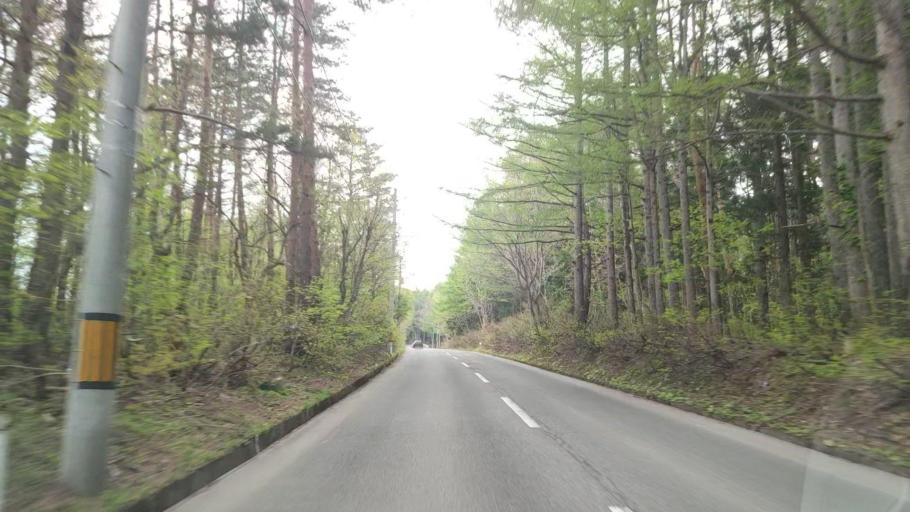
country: JP
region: Aomori
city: Aomori Shi
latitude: 40.7464
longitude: 140.8225
